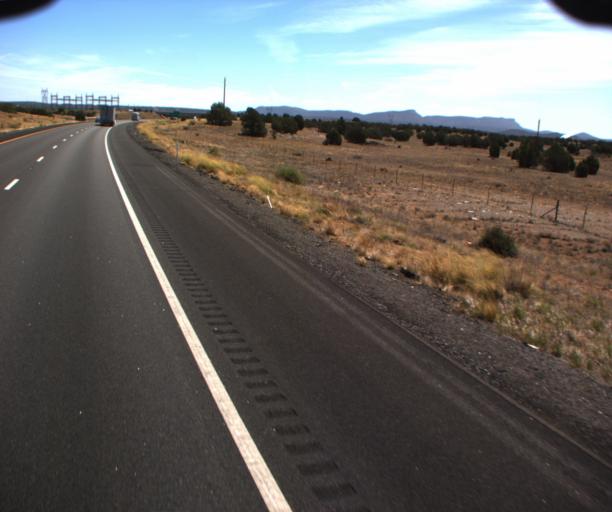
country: US
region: Arizona
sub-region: Mohave County
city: Peach Springs
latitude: 35.1897
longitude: -113.3728
